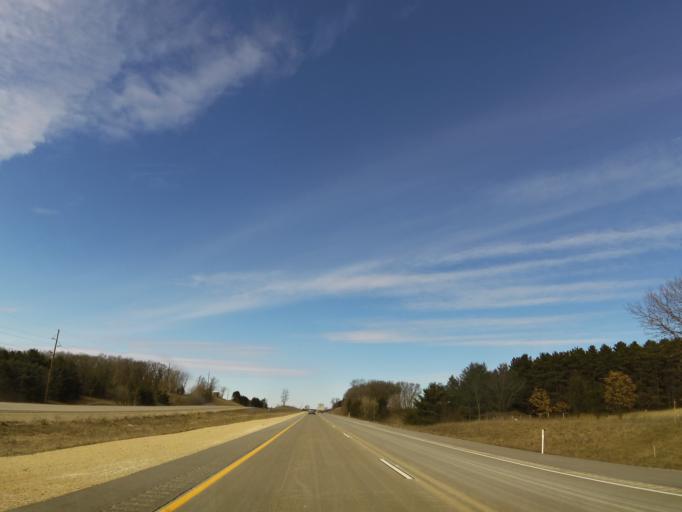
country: US
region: Wisconsin
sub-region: Monroe County
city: Tomah
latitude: 44.0847
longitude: -90.5276
